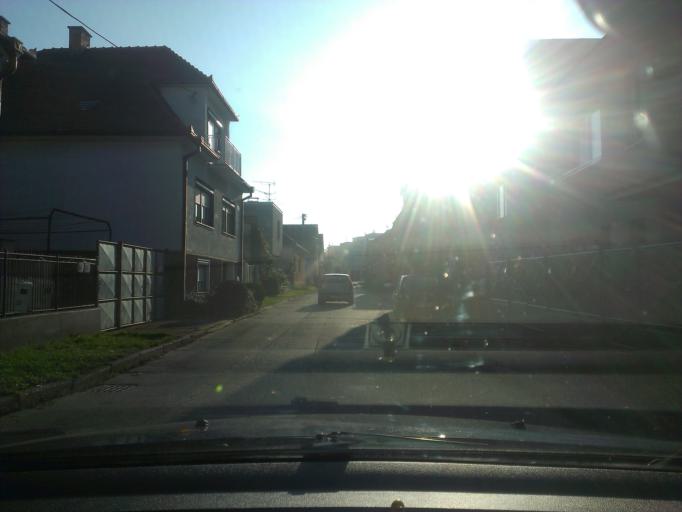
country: SK
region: Trnavsky
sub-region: Okres Trnava
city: Piestany
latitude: 48.5899
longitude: 17.8172
